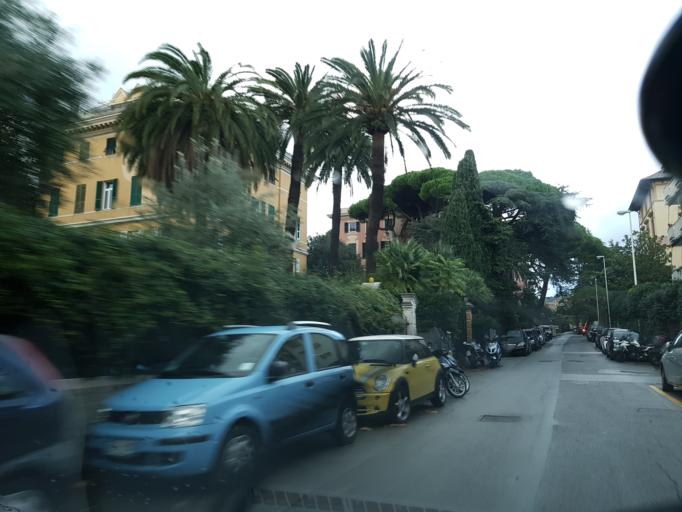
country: IT
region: Liguria
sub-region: Provincia di Genova
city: Genoa
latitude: 44.3984
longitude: 8.9690
